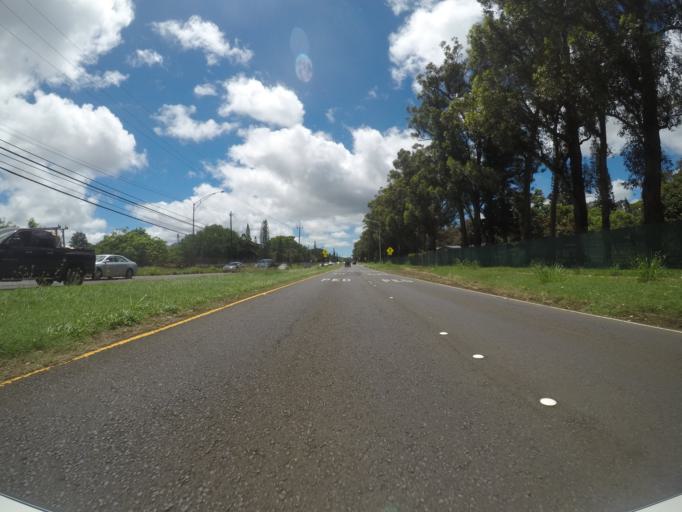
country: US
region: Hawaii
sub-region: Honolulu County
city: Wahiawa
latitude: 21.4896
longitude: -158.0437
